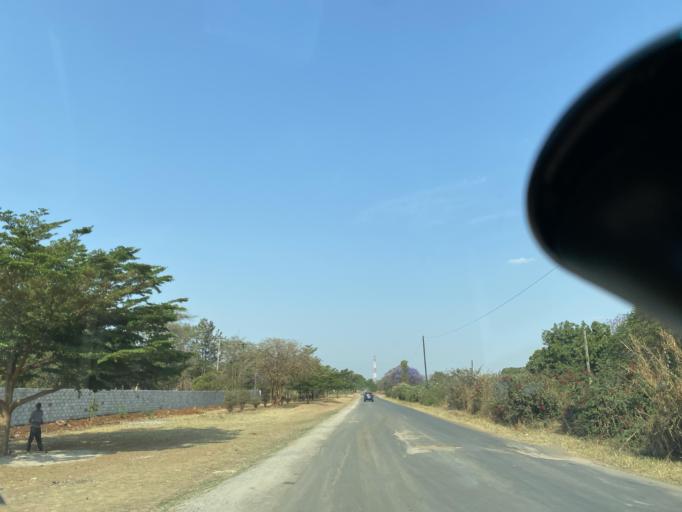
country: ZM
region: Lusaka
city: Lusaka
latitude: -15.4816
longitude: 28.1768
